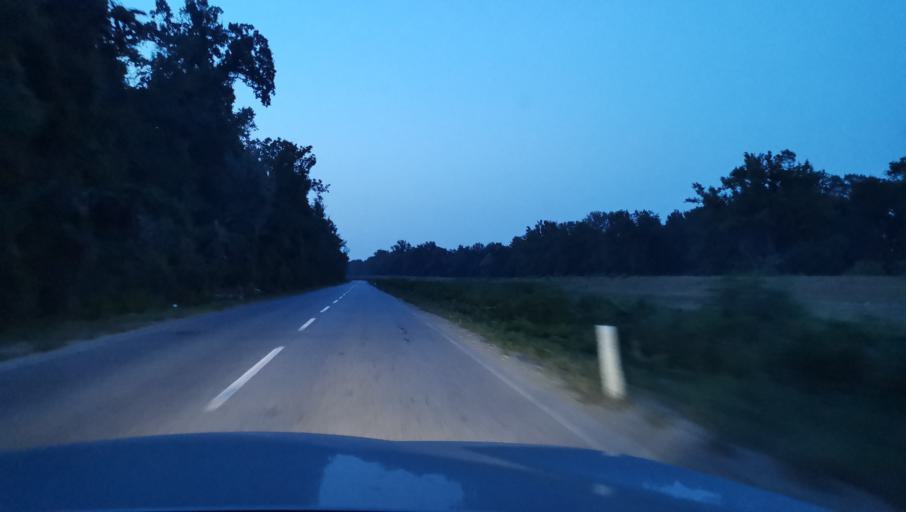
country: RS
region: Central Serbia
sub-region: Belgrade
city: Obrenovac
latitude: 44.6847
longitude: 20.1930
